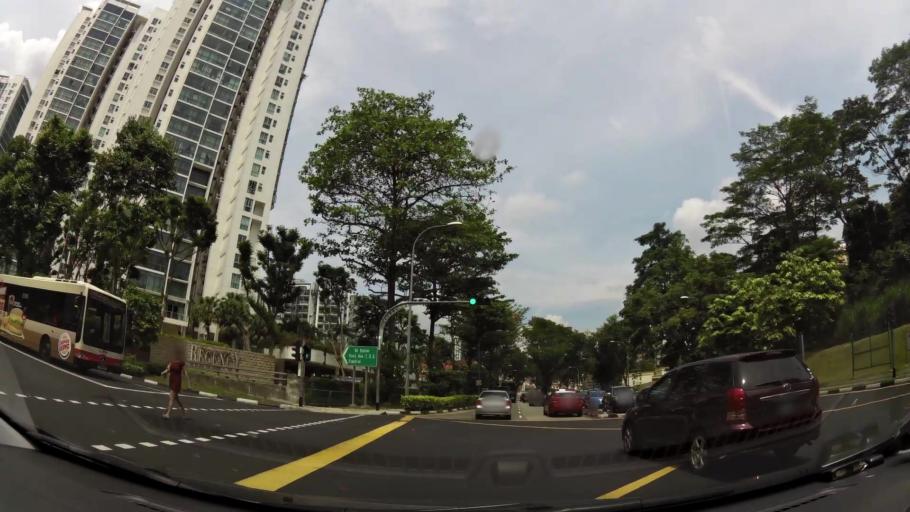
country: SG
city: Singapore
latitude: 1.3518
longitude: 103.7599
